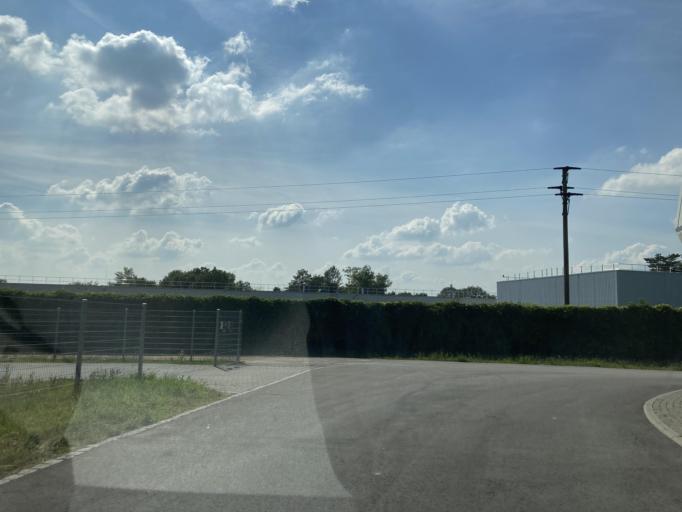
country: DE
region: Baden-Wuerttemberg
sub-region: Freiburg Region
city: Neuenburg am Rhein
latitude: 47.8047
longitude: 7.5599
